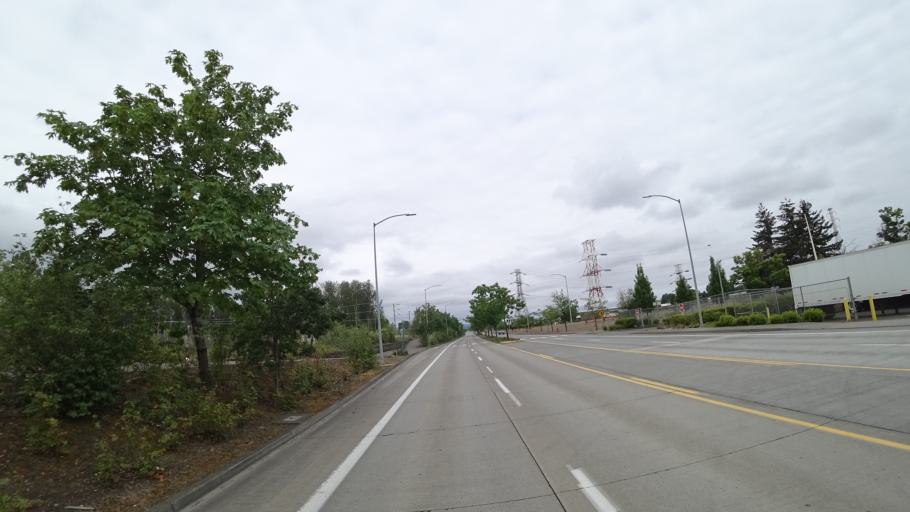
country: US
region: Washington
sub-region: Clark County
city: Vancouver
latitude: 45.6205
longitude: -122.7275
